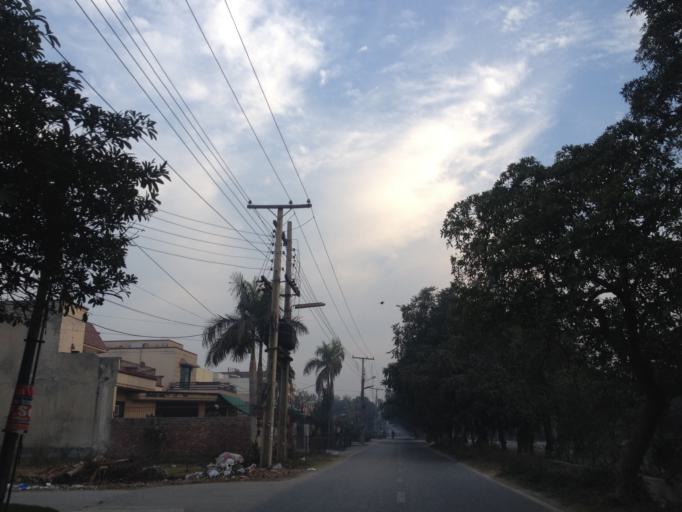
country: PK
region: Punjab
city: Lahore
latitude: 31.4610
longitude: 74.2995
